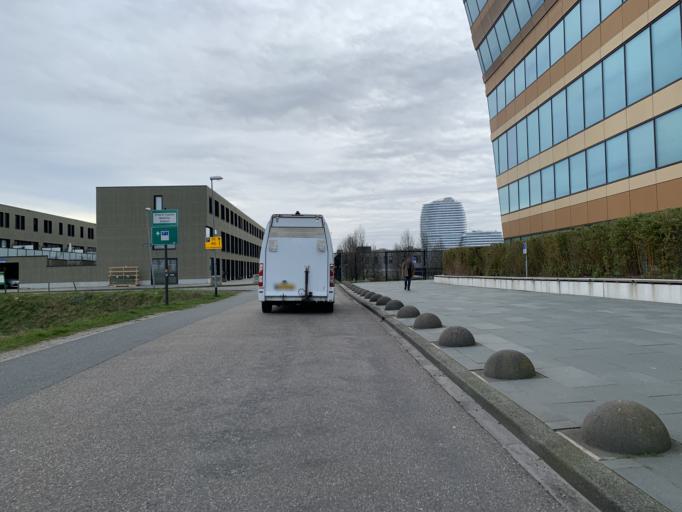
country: NL
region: Groningen
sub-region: Gemeente Groningen
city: Oosterpark
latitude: 53.2089
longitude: 6.5887
